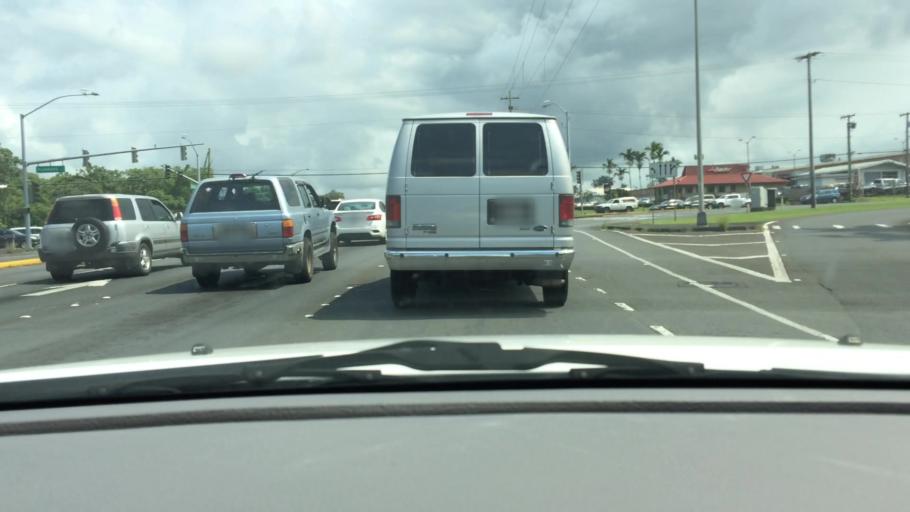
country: US
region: Hawaii
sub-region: Hawaii County
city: Hilo
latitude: 19.6958
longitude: -155.0657
